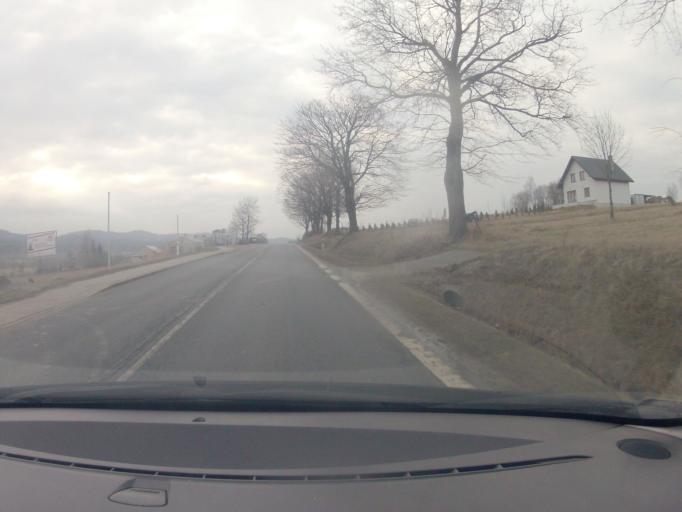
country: PL
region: Subcarpathian Voivodeship
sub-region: Powiat krosnienski
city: Dukla
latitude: 49.5603
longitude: 21.6169
